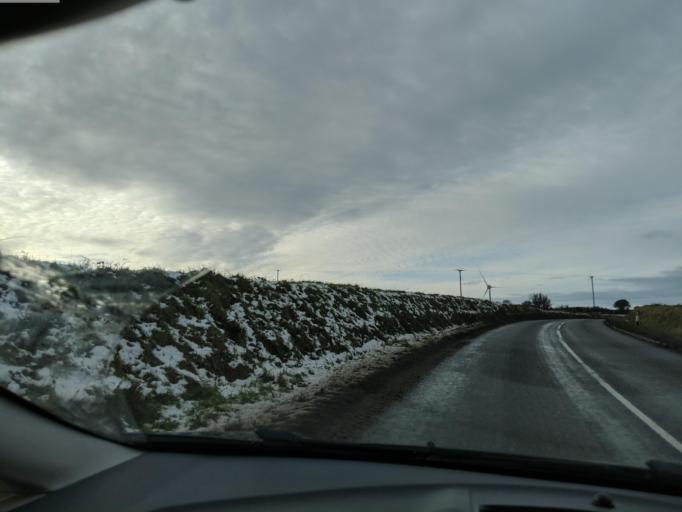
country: GB
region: England
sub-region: Cornwall
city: Jacobstow
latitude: 50.6641
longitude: -4.5877
